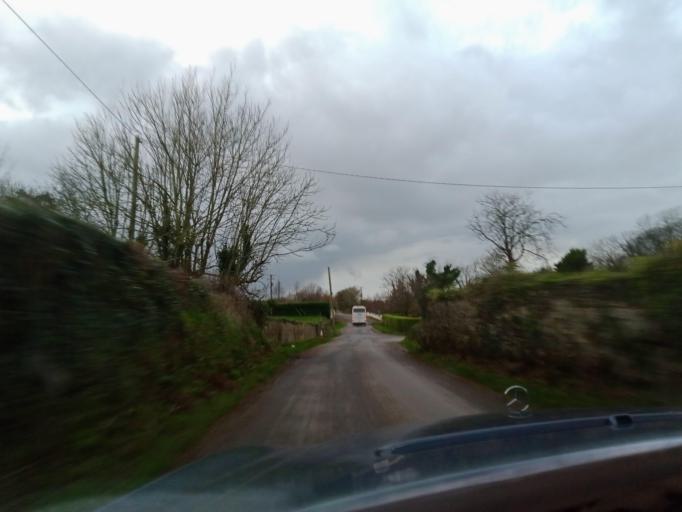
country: IE
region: Munster
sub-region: Waterford
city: Waterford
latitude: 52.3434
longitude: -7.0376
